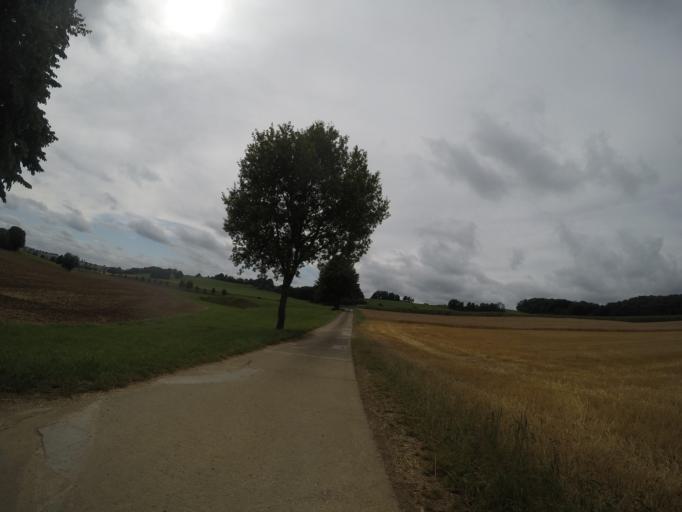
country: DE
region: Baden-Wuerttemberg
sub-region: Tuebingen Region
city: Laichingen
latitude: 48.4598
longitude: 9.6497
